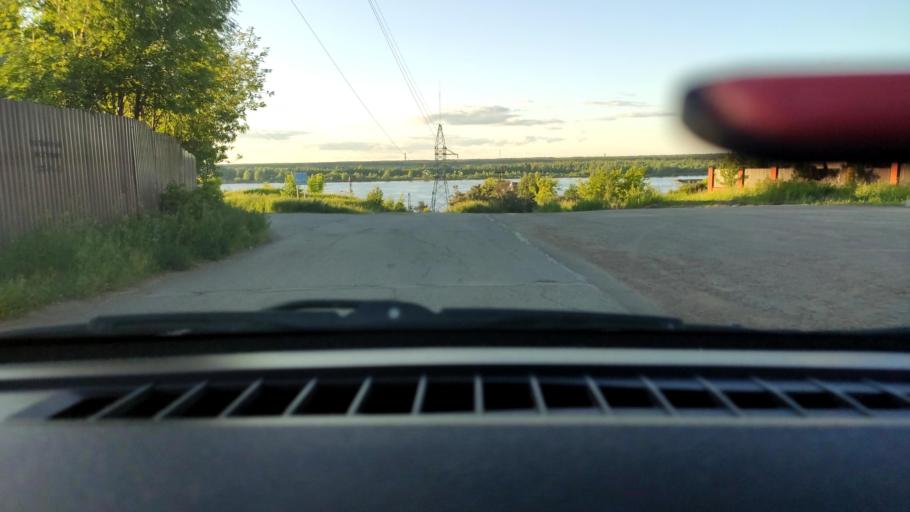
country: RU
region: Perm
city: Kultayevo
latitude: 57.9354
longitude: 55.8647
